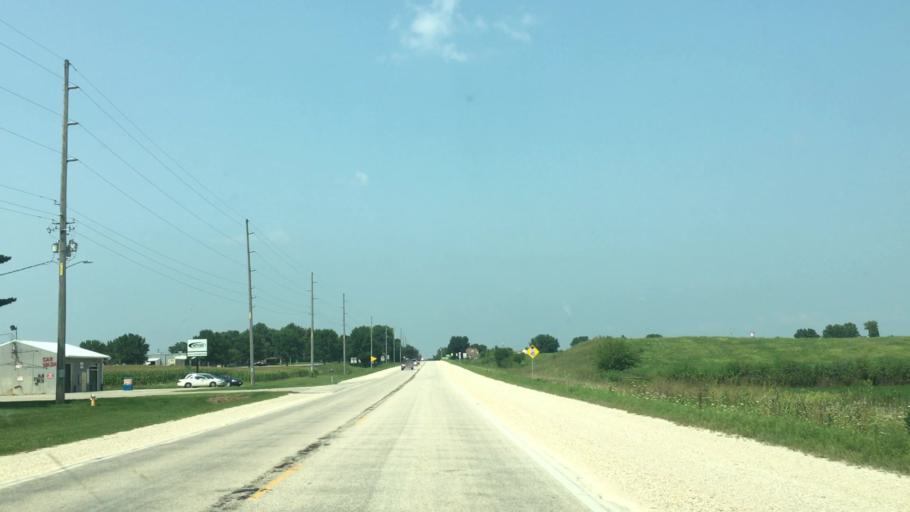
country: US
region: Iowa
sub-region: Fayette County
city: West Union
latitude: 42.9453
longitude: -91.8142
